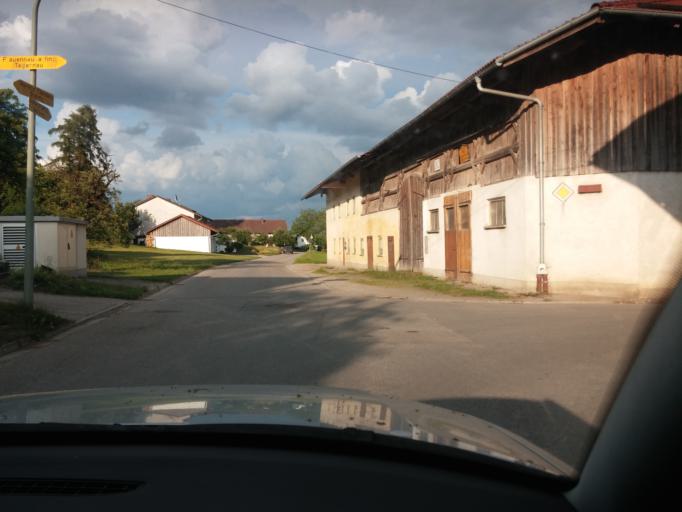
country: DE
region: Bavaria
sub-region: Upper Bavaria
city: Steinhoring
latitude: 48.0595
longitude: 12.0180
